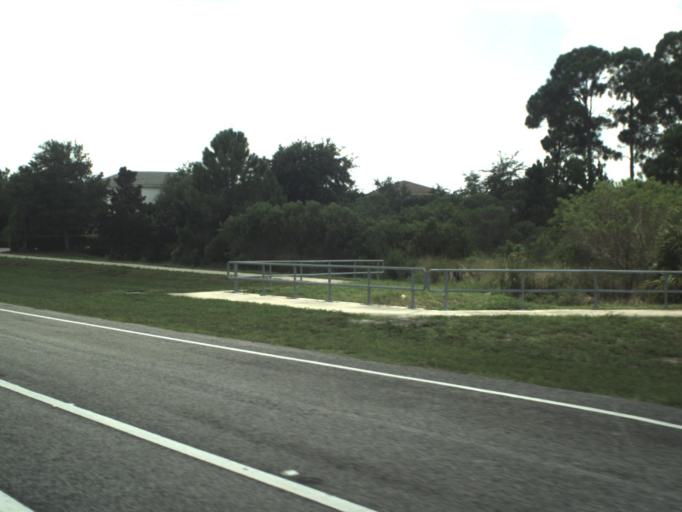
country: US
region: Florida
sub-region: Martin County
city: Port Salerno
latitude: 27.1116
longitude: -80.1724
